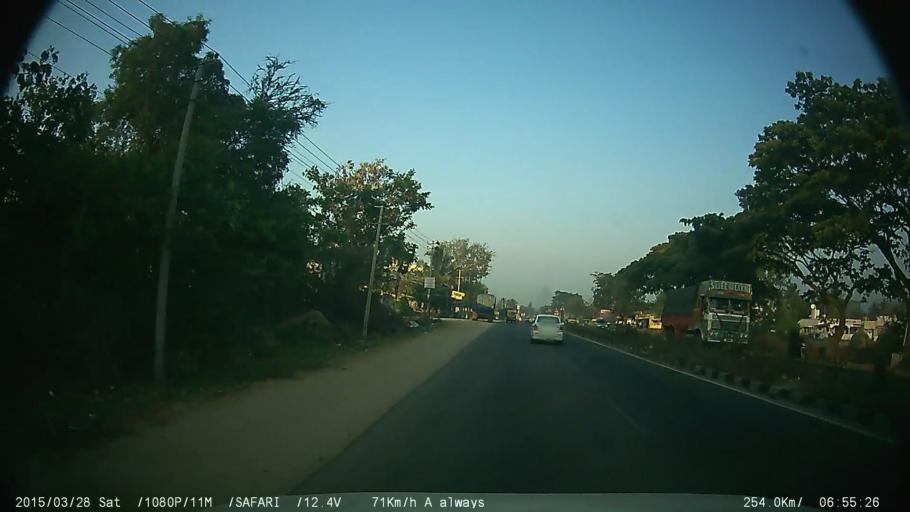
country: IN
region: Karnataka
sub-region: Mandya
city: Maddur
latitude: 12.5745
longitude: 77.0161
